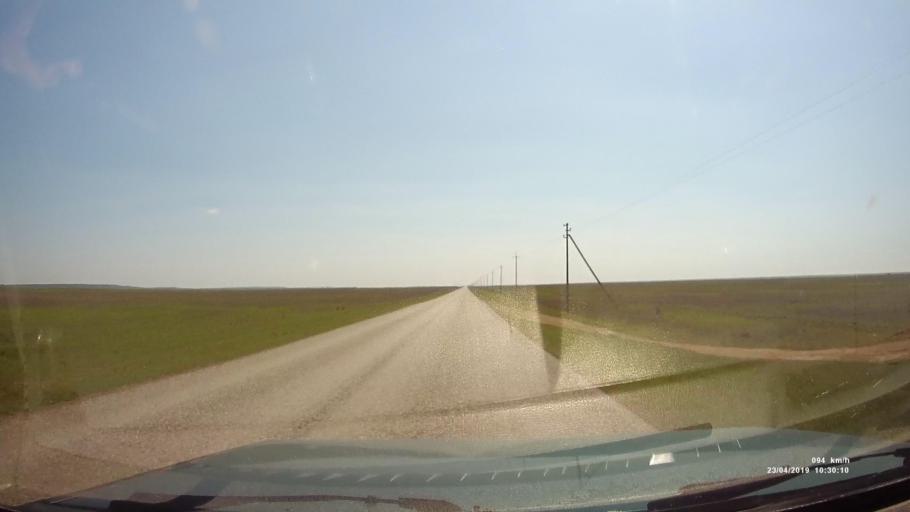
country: RU
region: Kalmykiya
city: Yashalta
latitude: 46.5939
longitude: 42.5392
